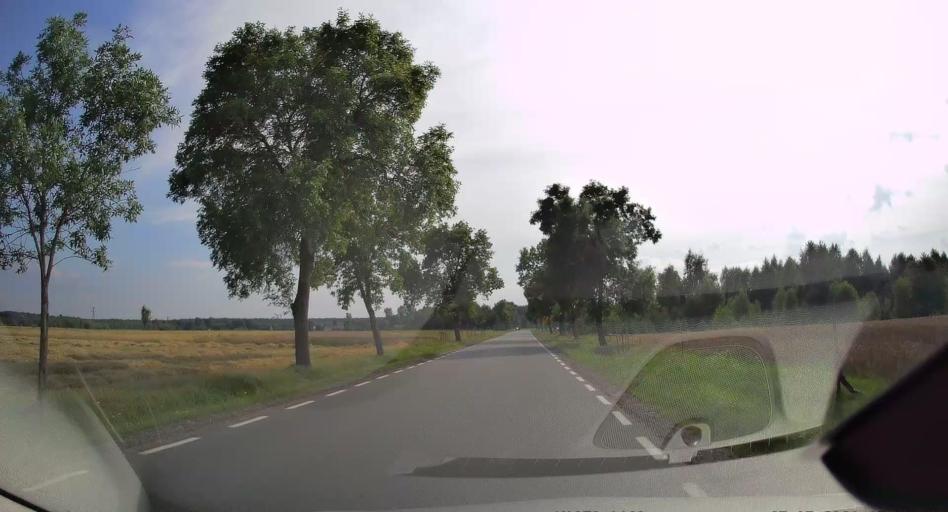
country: PL
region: Lodz Voivodeship
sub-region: Powiat tomaszowski
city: Rzeczyca
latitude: 51.5601
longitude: 20.2627
